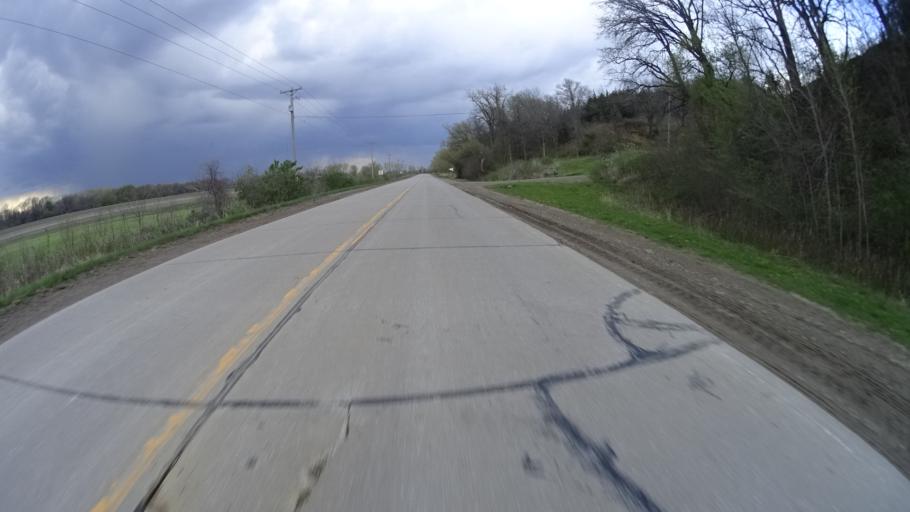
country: US
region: Iowa
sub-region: Mills County
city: Glenwood
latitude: 41.0744
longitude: -95.8126
